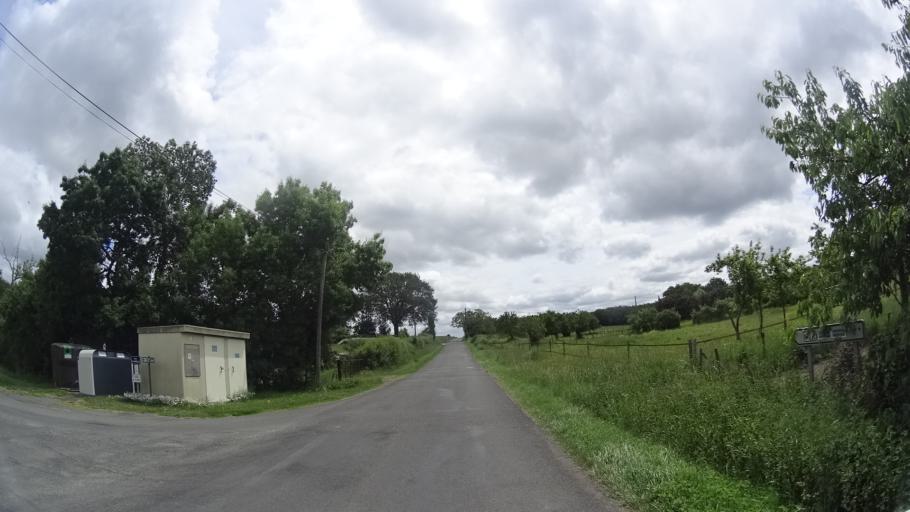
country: FR
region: Pays de la Loire
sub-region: Departement de Maine-et-Loire
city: Chenehutte-Treves-Cunault
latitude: 47.2912
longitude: -0.1476
